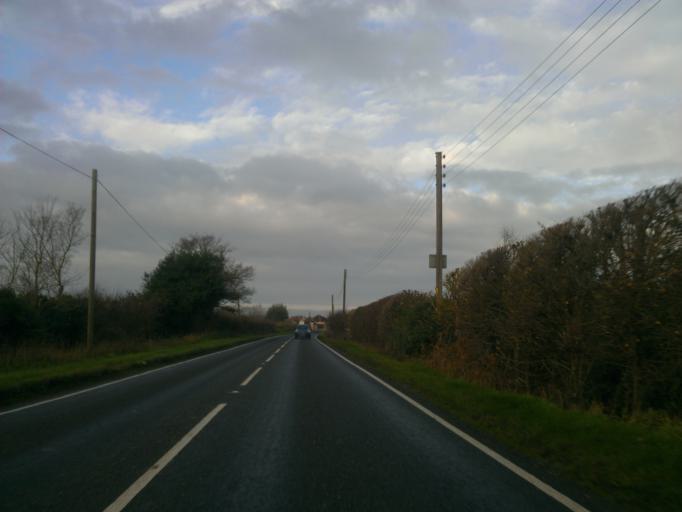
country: GB
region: England
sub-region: Essex
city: Great Bentley
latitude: 51.8375
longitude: 1.0463
